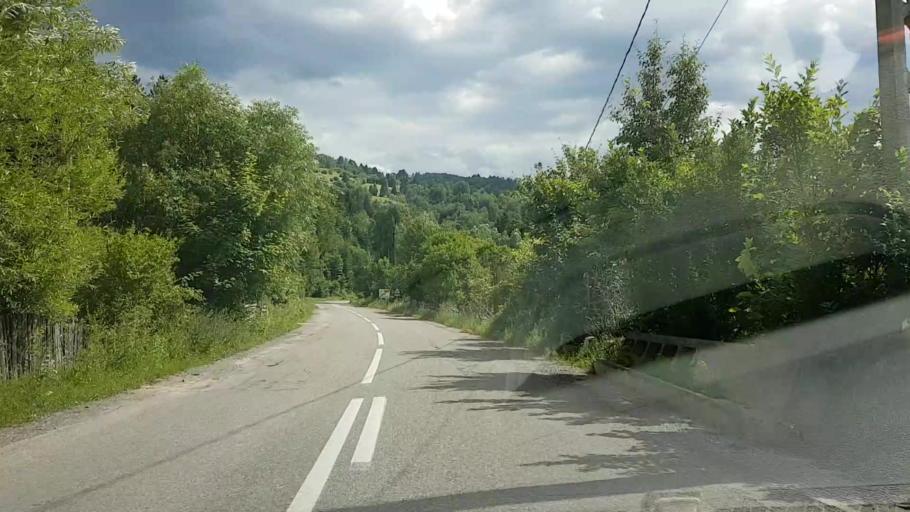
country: RO
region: Neamt
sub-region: Comuna Poiana Teiului
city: Poiana Teiului
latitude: 47.0843
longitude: 25.9698
